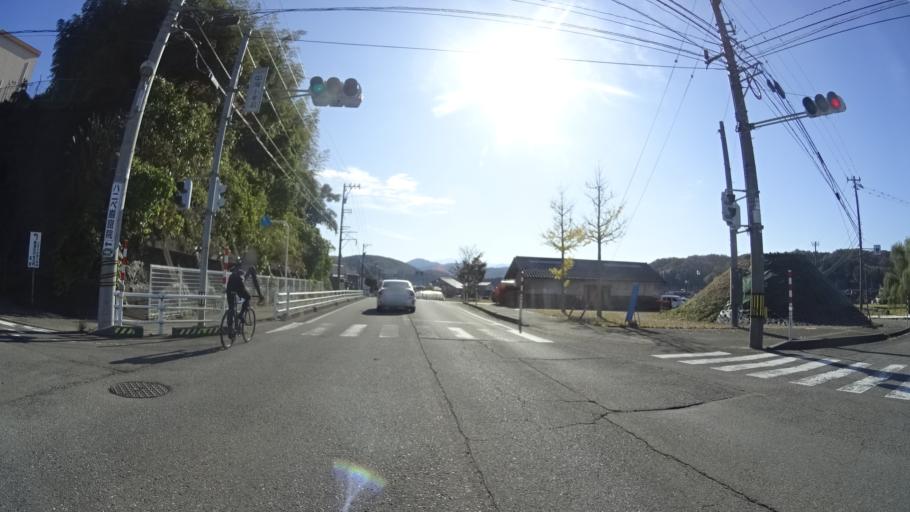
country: JP
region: Ishikawa
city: Komatsu
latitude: 36.3972
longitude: 136.5175
